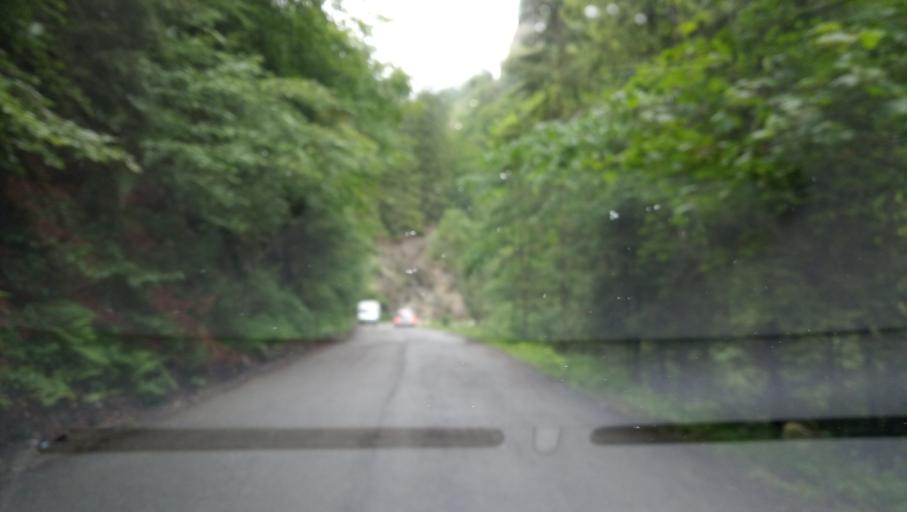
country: RO
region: Hunedoara
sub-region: Oras Petrila
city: Petrila
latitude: 45.4095
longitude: 23.4876
